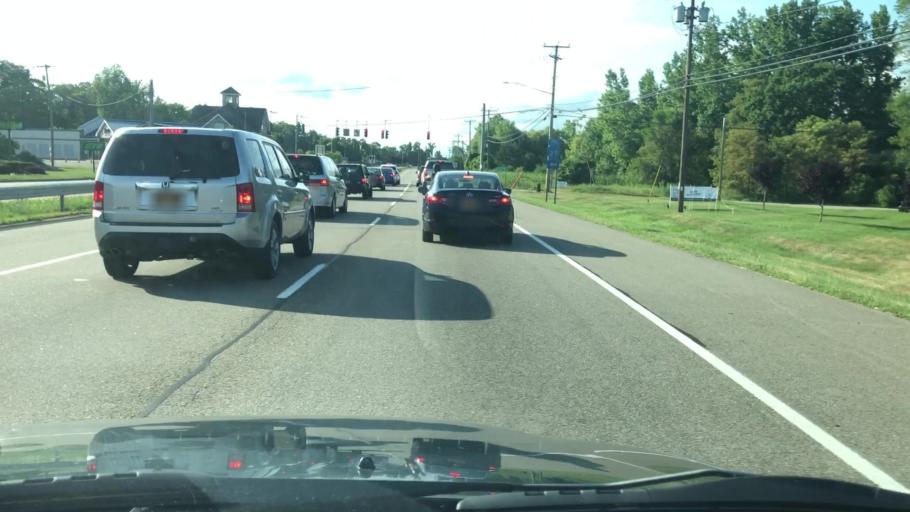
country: US
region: New York
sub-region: Dutchess County
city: Fishkill
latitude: 41.5638
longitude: -73.9048
